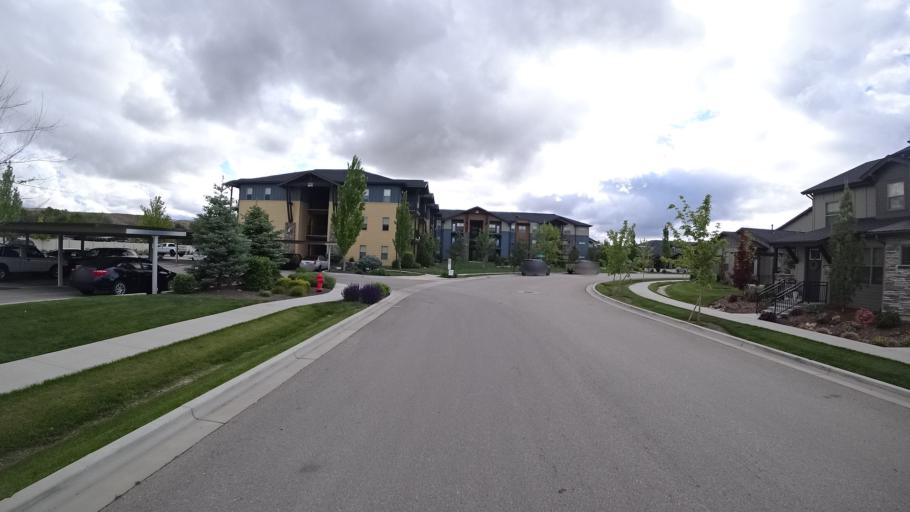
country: US
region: Idaho
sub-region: Ada County
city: Eagle
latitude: 43.6769
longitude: -116.2923
